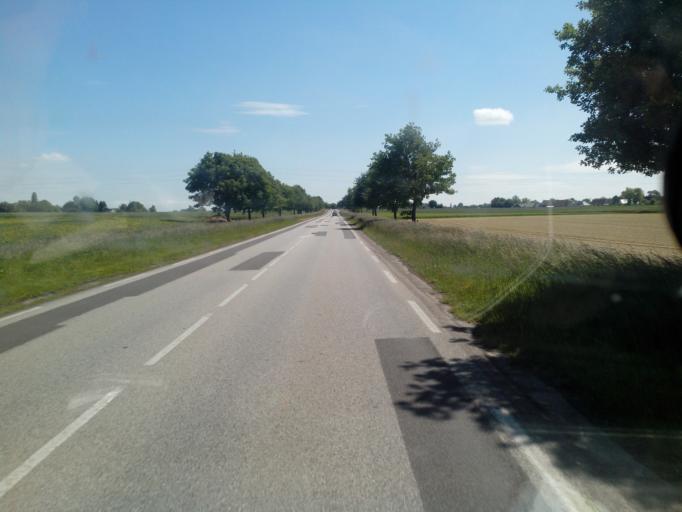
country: FR
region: Haute-Normandie
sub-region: Departement de l'Eure
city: Beuzeville
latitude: 49.3737
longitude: 0.3979
